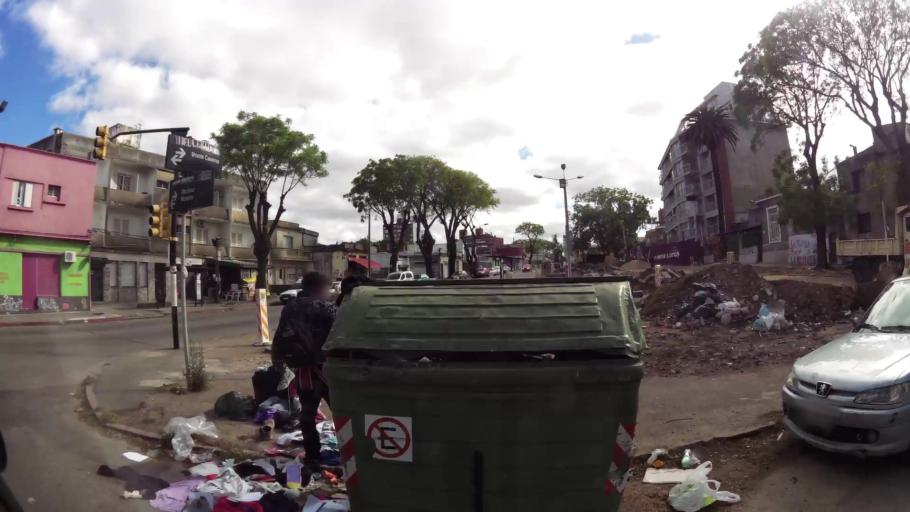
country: UY
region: Montevideo
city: Montevideo
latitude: -34.8810
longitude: -56.1576
